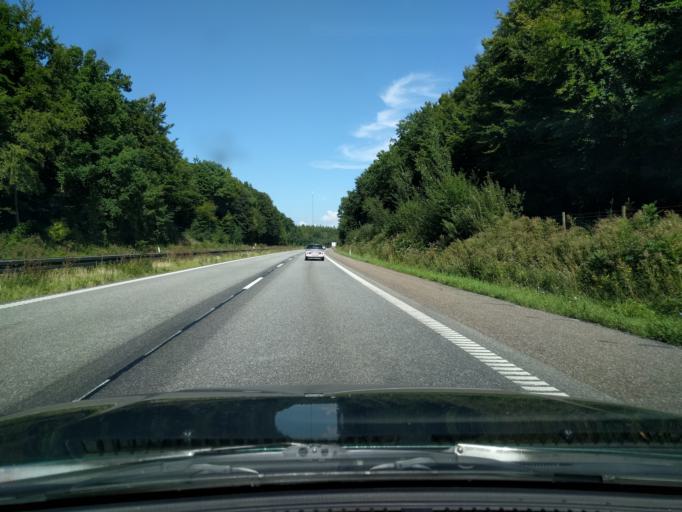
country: DK
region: Zealand
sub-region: Vordingborg Kommune
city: Orslev
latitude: 55.0214
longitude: 11.9845
